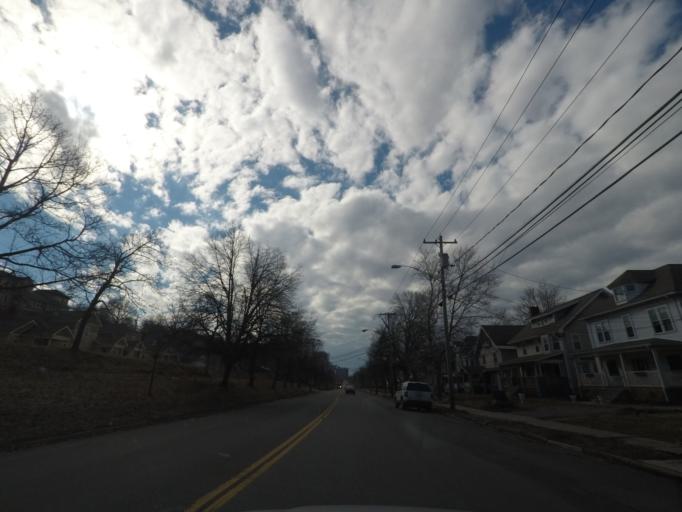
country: US
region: New York
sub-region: Onondaga County
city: Syracuse
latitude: 43.0471
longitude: -76.1243
